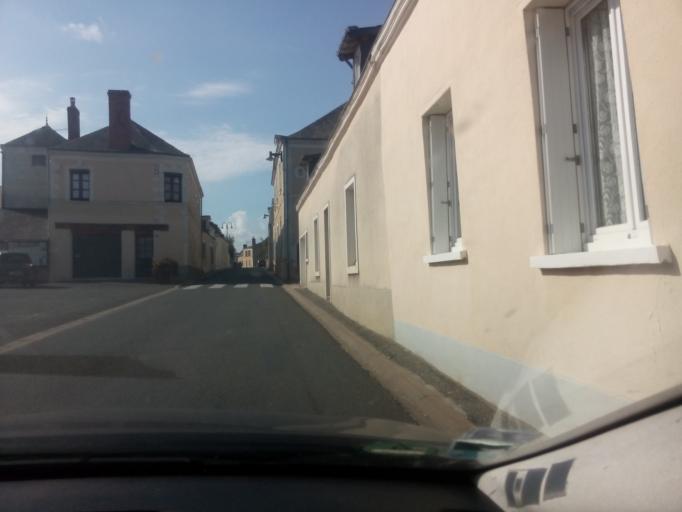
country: FR
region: Pays de la Loire
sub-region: Departement de Maine-et-Loire
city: Soulaire-et-Bourg
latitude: 47.5791
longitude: -0.5502
